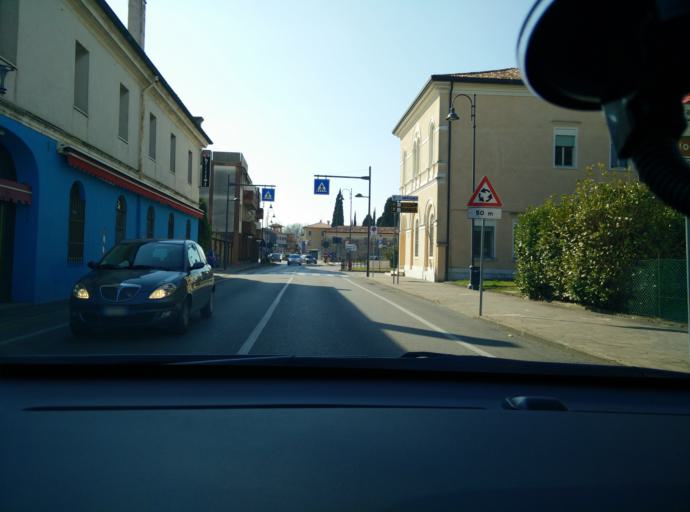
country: IT
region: Veneto
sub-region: Provincia di Venezia
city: Noventa di Piave
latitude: 45.6627
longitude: 12.5306
